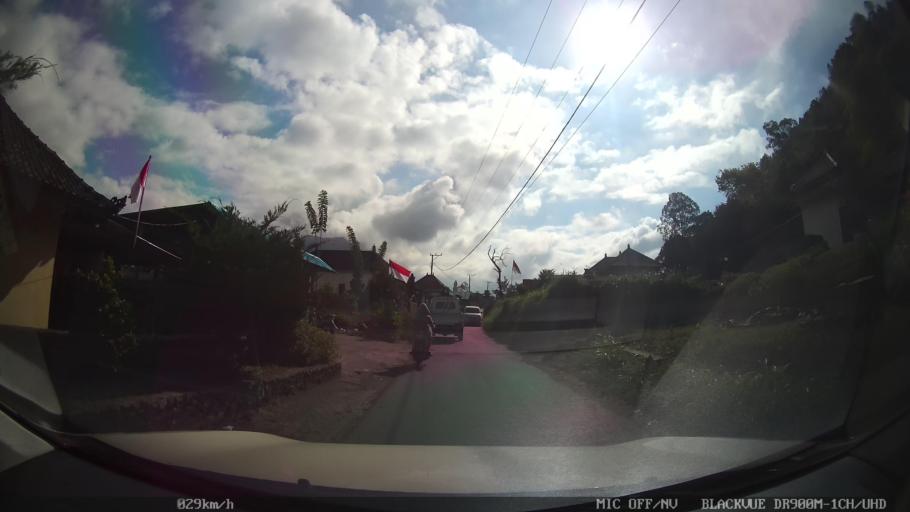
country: ID
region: Bali
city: Banjar Trunyan
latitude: -8.2265
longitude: 115.4038
